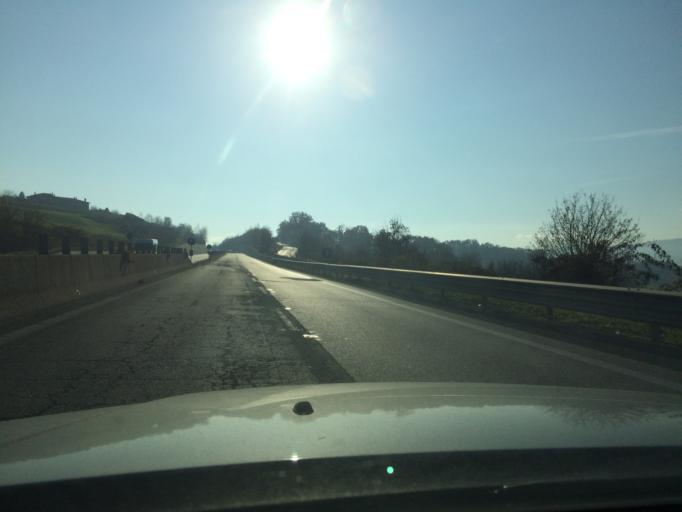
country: IT
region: Umbria
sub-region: Provincia di Perugia
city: Ponterio-Pian di Porto
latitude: 42.8302
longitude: 12.3999
